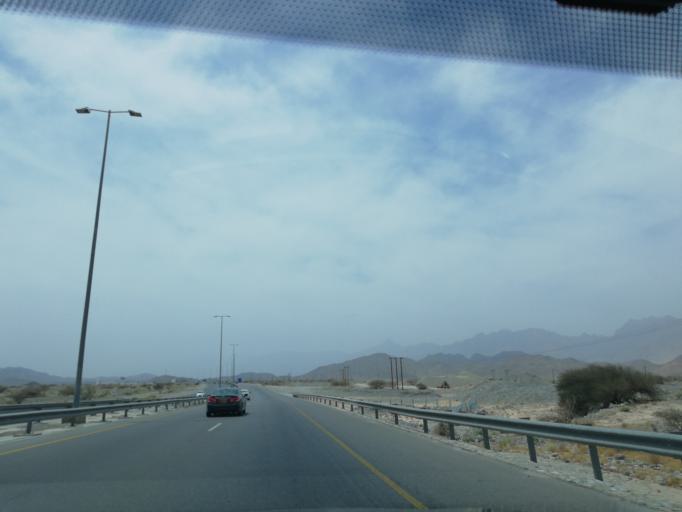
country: OM
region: Muhafazat ad Dakhiliyah
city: Bidbid
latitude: 23.3936
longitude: 58.0674
